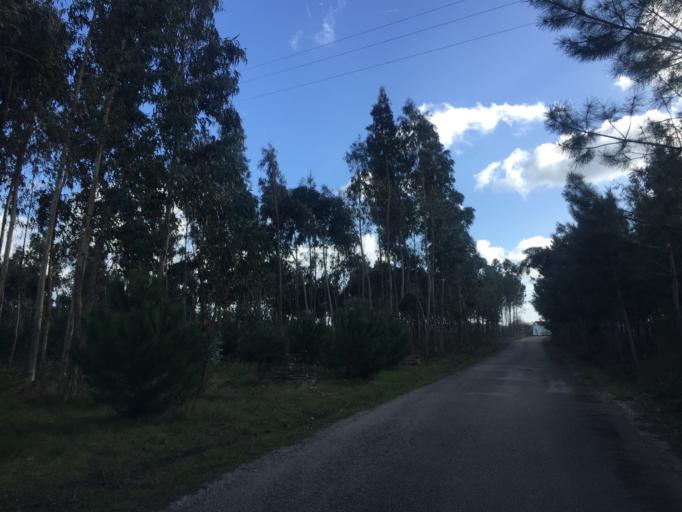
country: PT
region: Coimbra
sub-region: Figueira da Foz
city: Lavos
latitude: 40.0170
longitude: -8.8202
